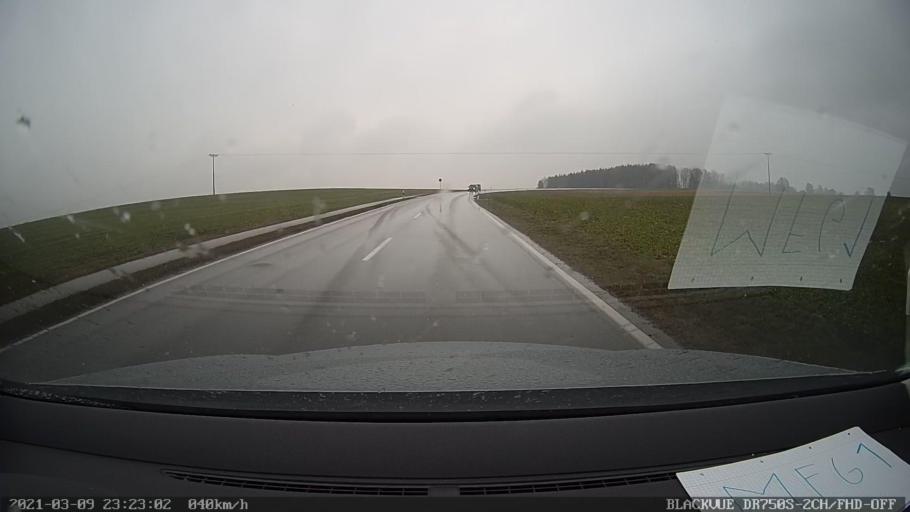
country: DE
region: Bavaria
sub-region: Upper Bavaria
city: Schonstett
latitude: 47.9844
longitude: 12.2500
